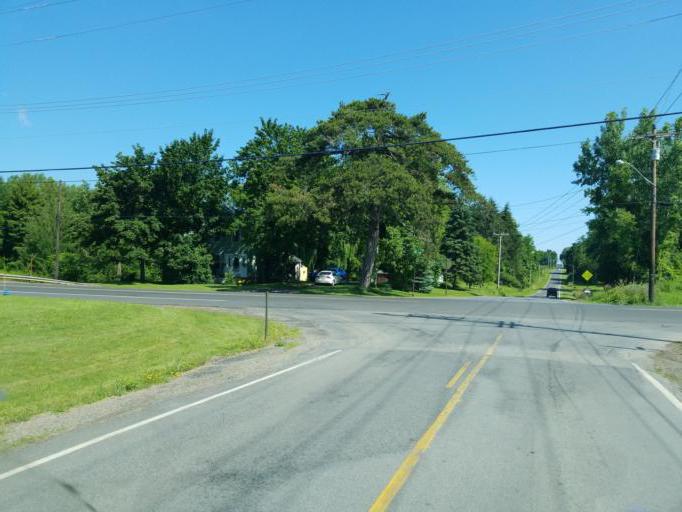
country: US
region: New York
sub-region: Wayne County
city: Wolcott
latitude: 43.2238
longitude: -76.8800
